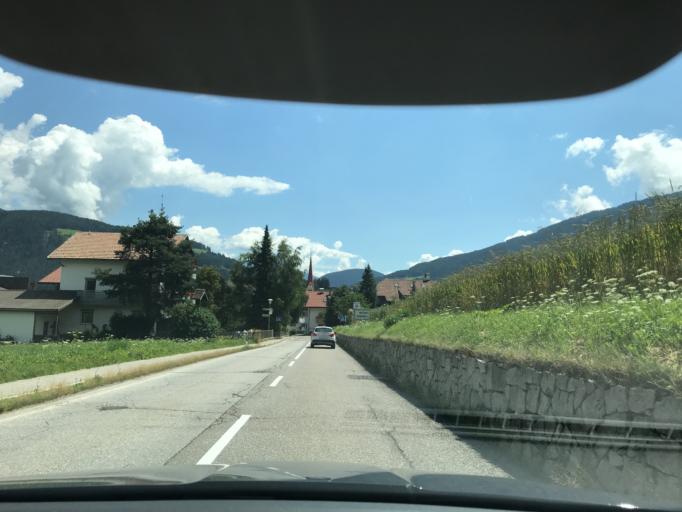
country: IT
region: Trentino-Alto Adige
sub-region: Bolzano
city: Valdaora di Mezzo
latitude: 46.7600
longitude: 12.0259
